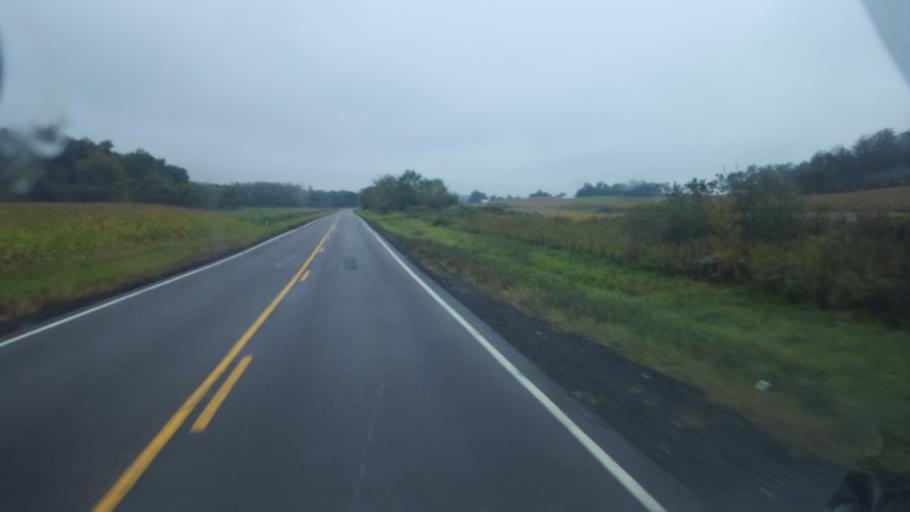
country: US
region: Ohio
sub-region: Sandusky County
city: Bellville
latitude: 40.5441
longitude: -82.4896
